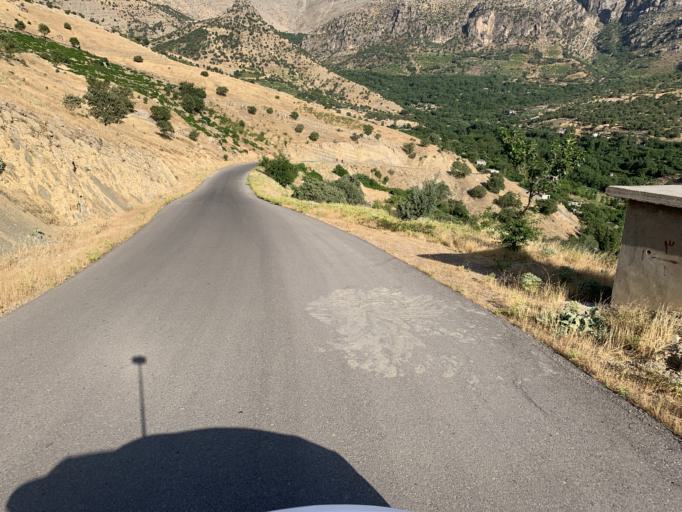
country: IQ
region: As Sulaymaniyah
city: Qeladize
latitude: 35.9947
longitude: 45.1931
